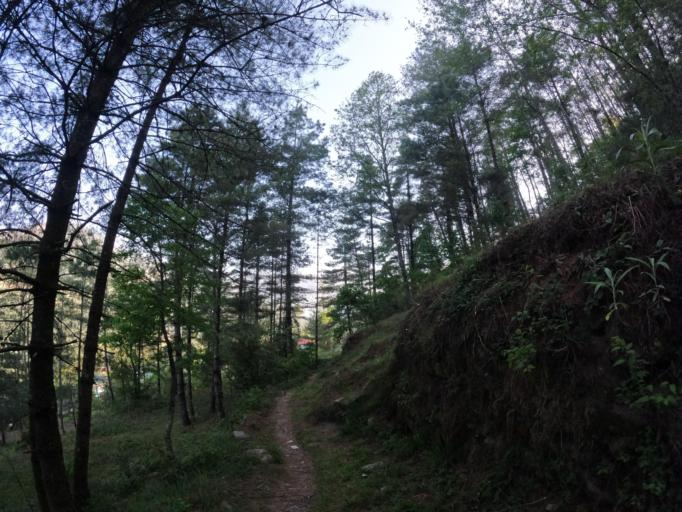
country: NP
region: Eastern Region
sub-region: Sagarmatha Zone
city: Namche Bazar
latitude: 27.4889
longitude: 86.5815
